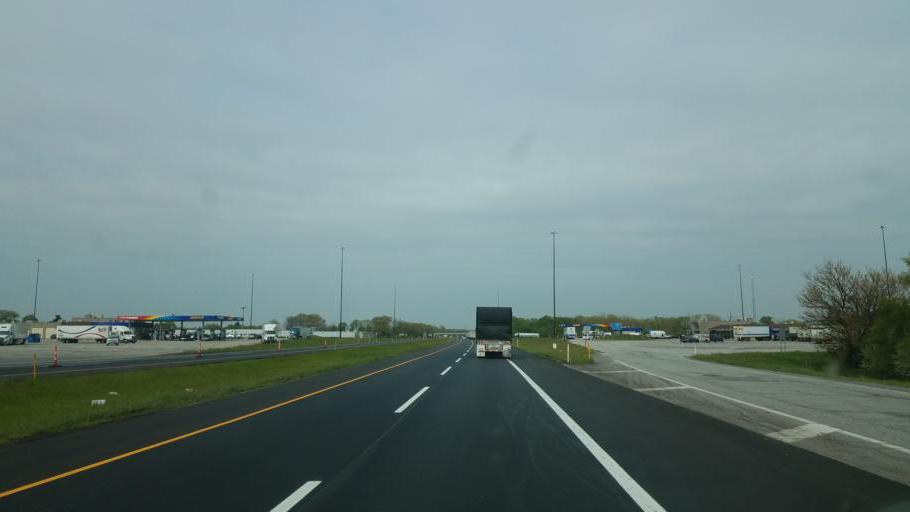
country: US
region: Indiana
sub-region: Elkhart County
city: Simonton Lake
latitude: 41.7322
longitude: -86.0016
